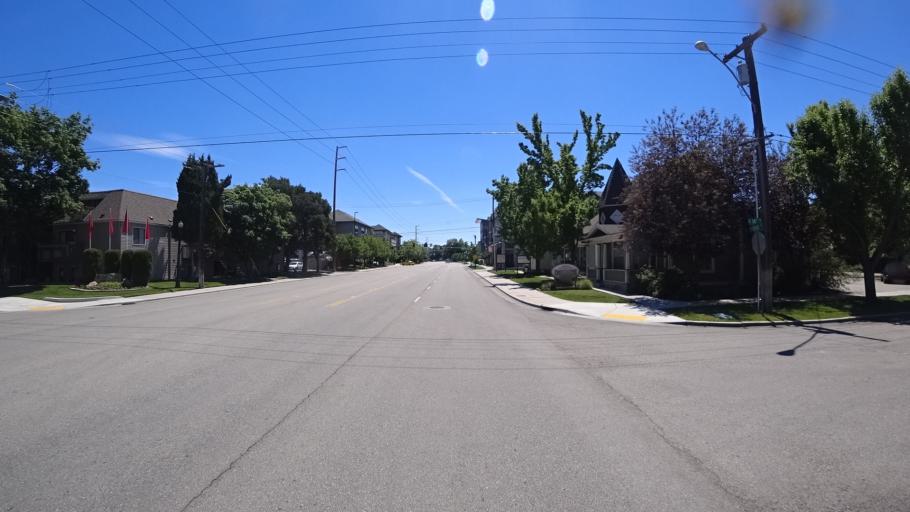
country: US
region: Idaho
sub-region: Ada County
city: Boise
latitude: 43.6160
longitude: -116.2156
